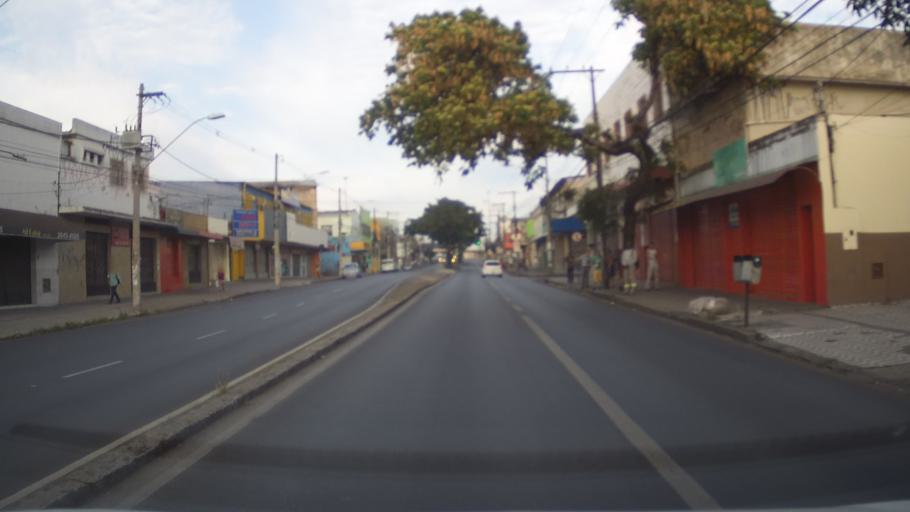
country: BR
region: Minas Gerais
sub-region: Belo Horizonte
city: Belo Horizonte
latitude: -19.9141
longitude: -43.9900
